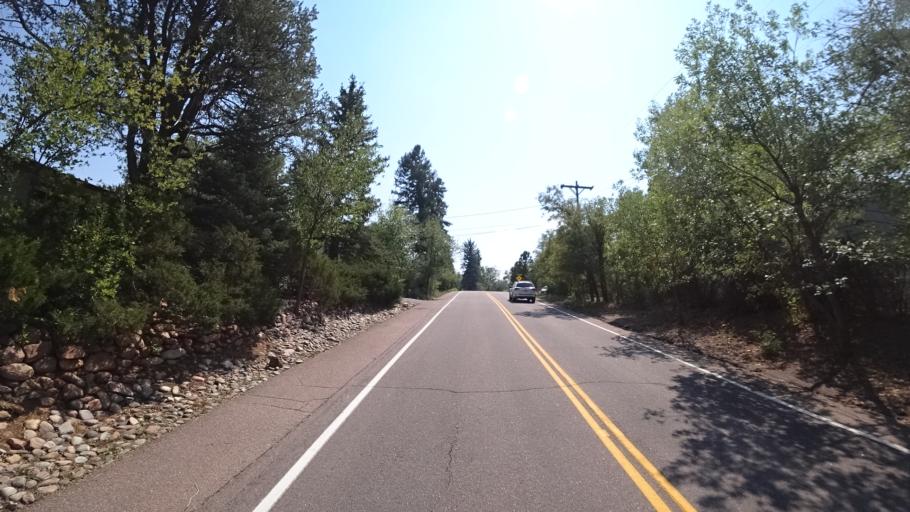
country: US
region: Colorado
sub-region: El Paso County
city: Colorado Springs
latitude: 38.7997
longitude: -104.8352
